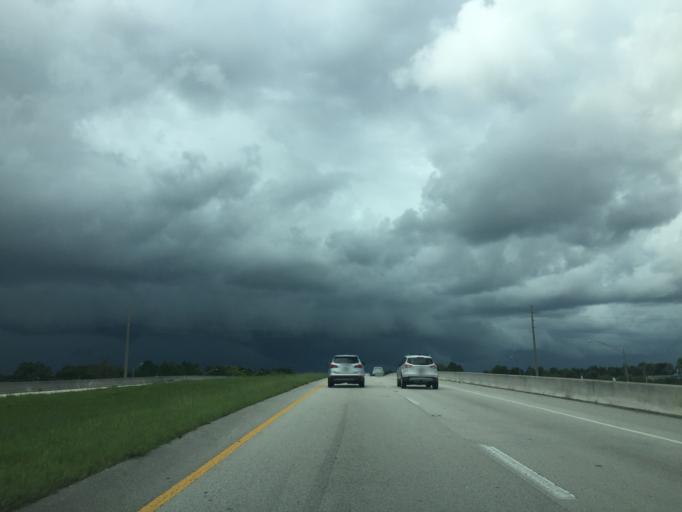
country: US
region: Florida
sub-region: Orange County
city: Lockhart
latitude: 28.6408
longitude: -81.4138
